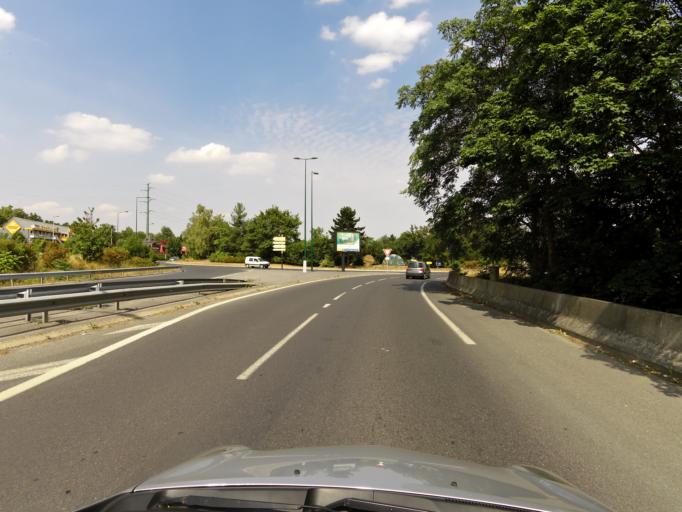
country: FR
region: Champagne-Ardenne
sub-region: Departement de la Marne
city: Bezannes
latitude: 49.2121
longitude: 4.0147
